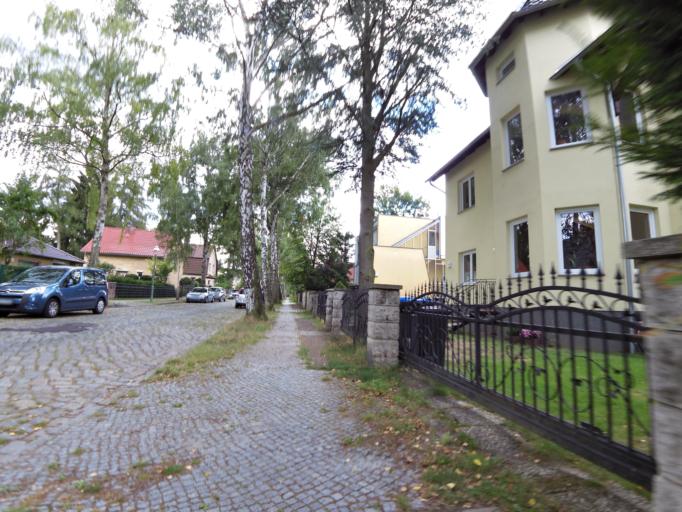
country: DE
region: Berlin
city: Lichtenrade
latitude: 52.3863
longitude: 13.3887
